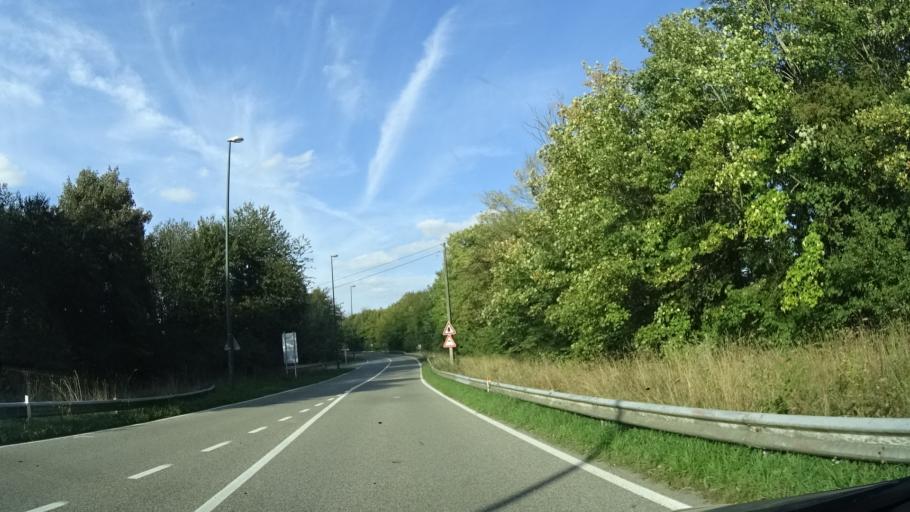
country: BE
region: Wallonia
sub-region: Province de Namur
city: Cerfontaine
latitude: 50.2185
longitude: 4.3826
